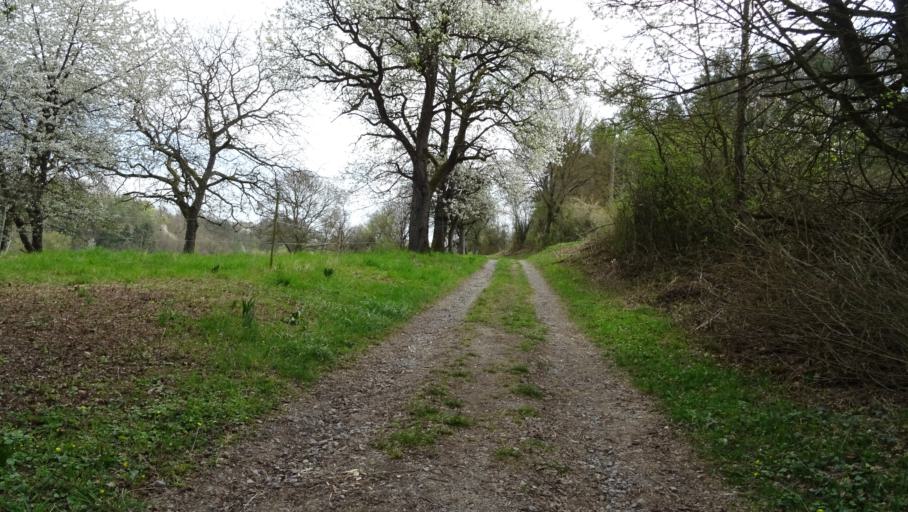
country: DE
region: Baden-Wuerttemberg
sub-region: Karlsruhe Region
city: Mosbach
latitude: 49.3741
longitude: 9.1708
